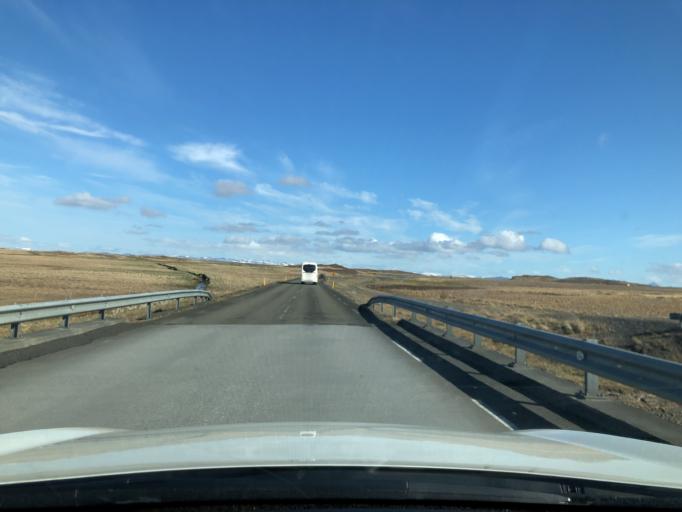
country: IS
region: West
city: Borgarnes
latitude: 64.5522
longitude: -21.7316
